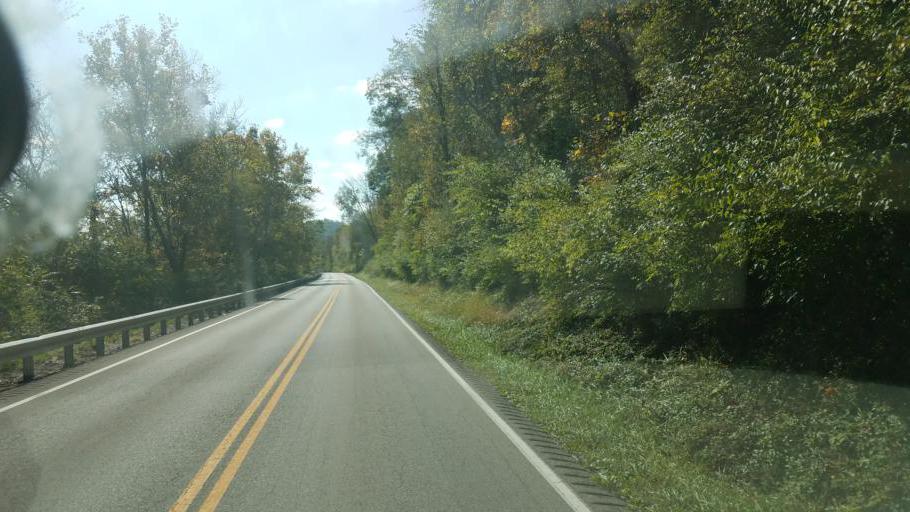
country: US
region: Ohio
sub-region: Brown County
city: Aberdeen
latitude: 38.6694
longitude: -83.7819
